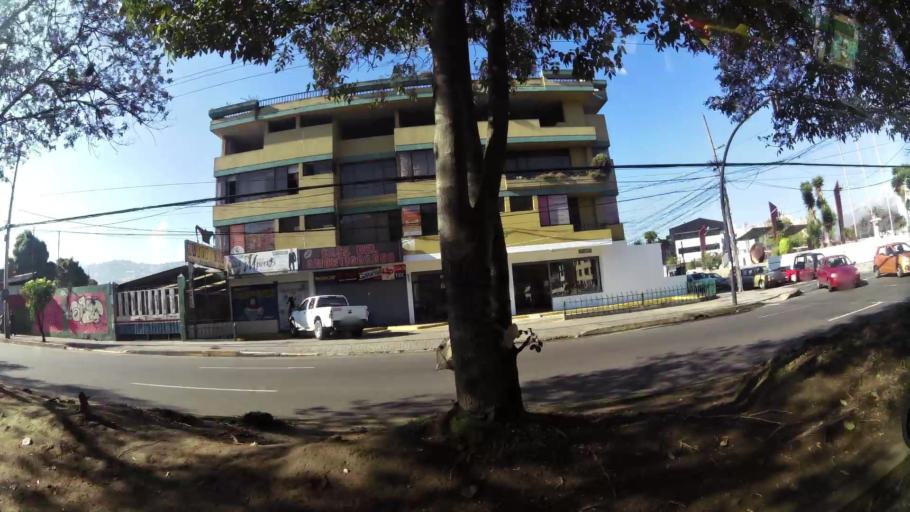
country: EC
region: Pichincha
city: Quito
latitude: -0.2474
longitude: -78.5247
